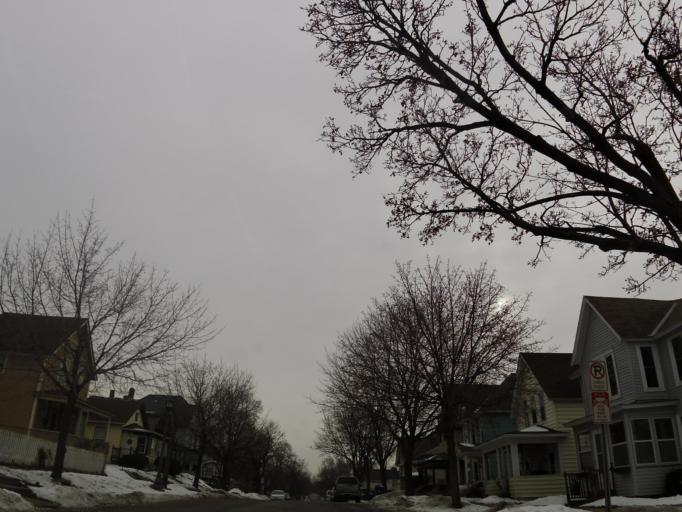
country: US
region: Minnesota
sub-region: Ramsey County
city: Saint Paul
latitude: 44.9577
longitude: -93.0710
